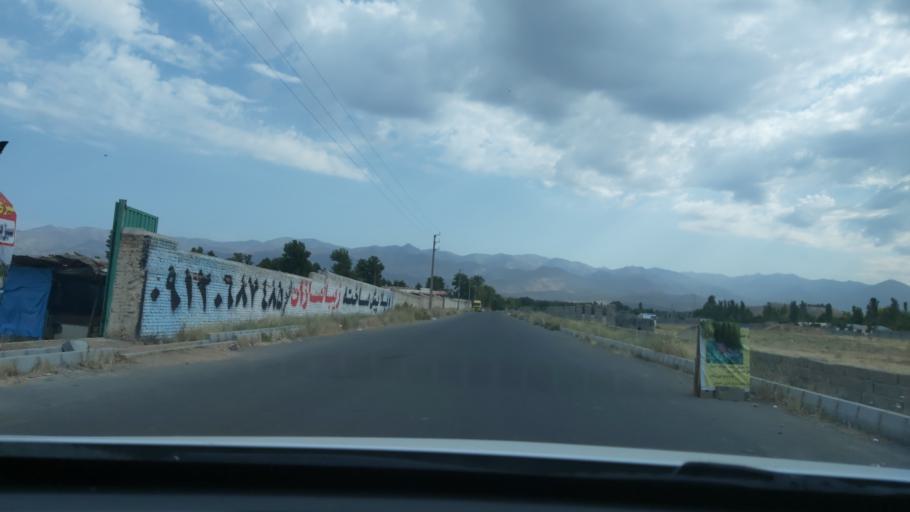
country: IR
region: Alborz
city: Hashtgerd
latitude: 35.9447
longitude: 50.7714
